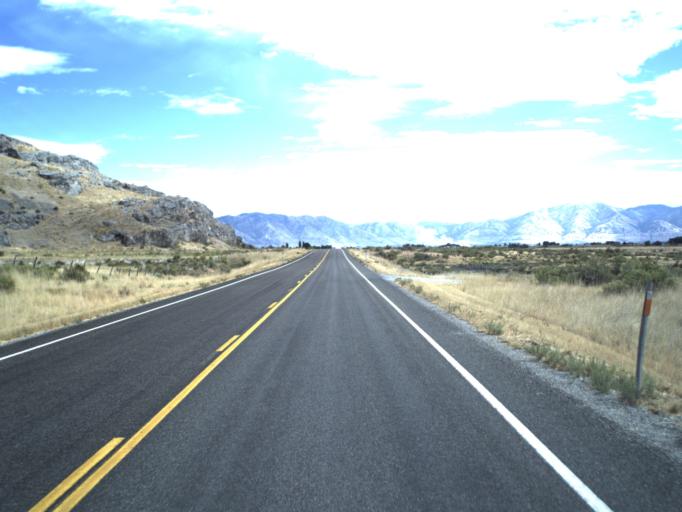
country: US
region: Utah
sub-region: Box Elder County
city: Elwood
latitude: 41.5776
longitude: -112.2386
